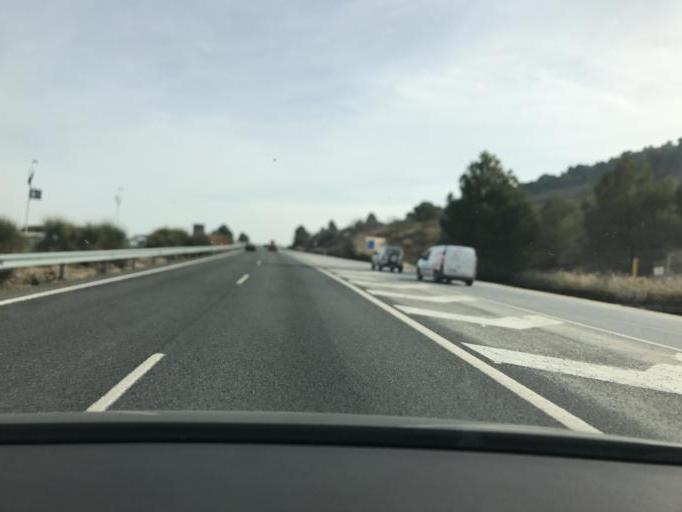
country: ES
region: Andalusia
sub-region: Provincia de Granada
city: Loja
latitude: 37.1648
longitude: -4.1673
